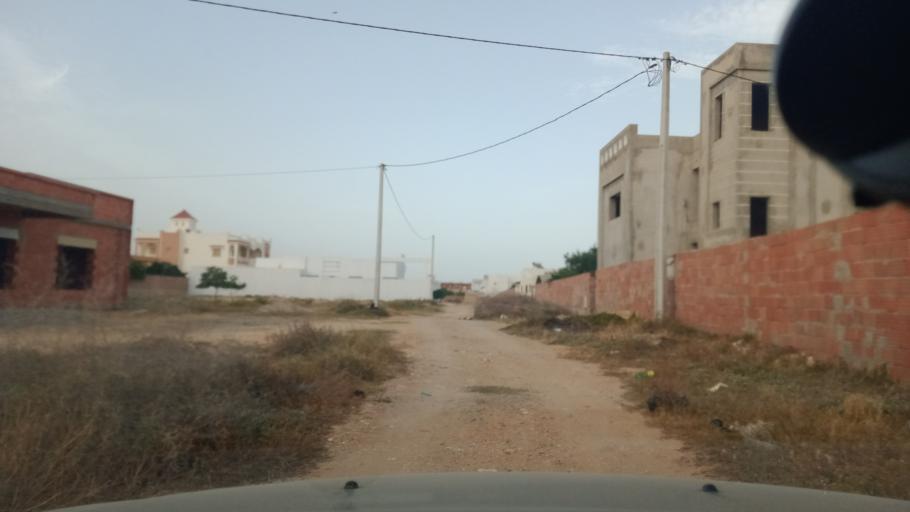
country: TN
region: Safaqis
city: Al Qarmadah
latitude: 34.7917
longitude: 10.7703
